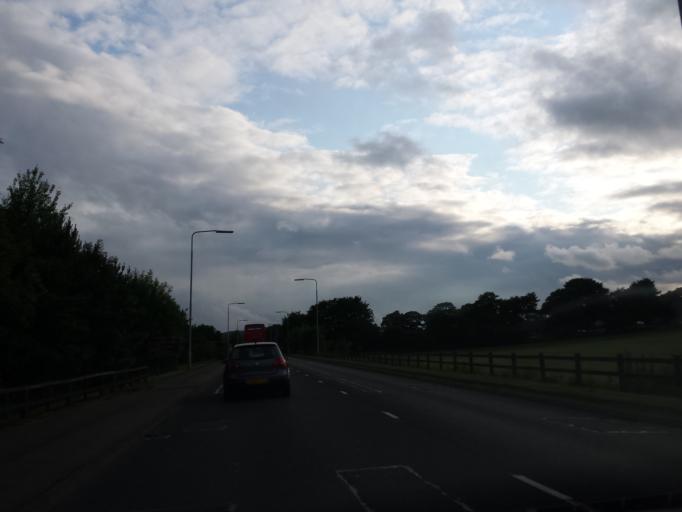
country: GB
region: Scotland
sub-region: Fife
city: Cupar
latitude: 56.3235
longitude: -2.9965
